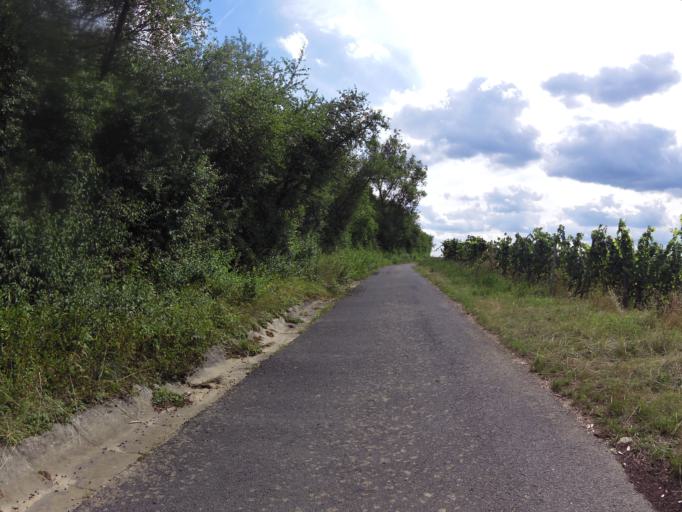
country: DE
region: Bavaria
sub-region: Regierungsbezirk Unterfranken
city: Sommerhausen
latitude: 49.6890
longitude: 10.0343
